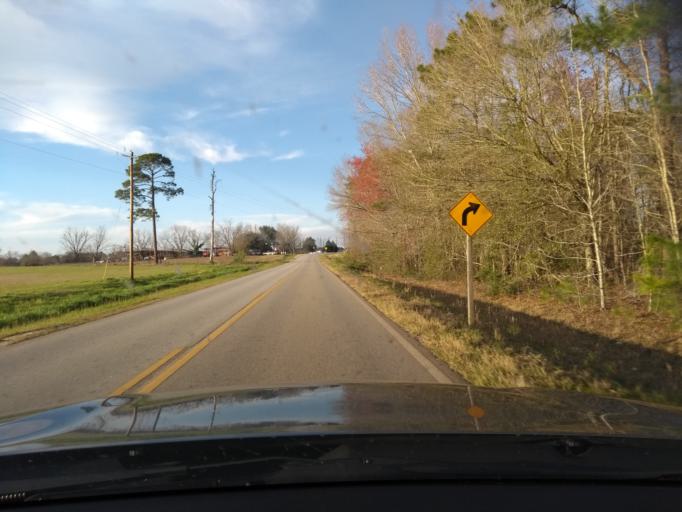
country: US
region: Georgia
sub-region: Bulloch County
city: Statesboro
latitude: 32.3560
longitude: -81.7712
